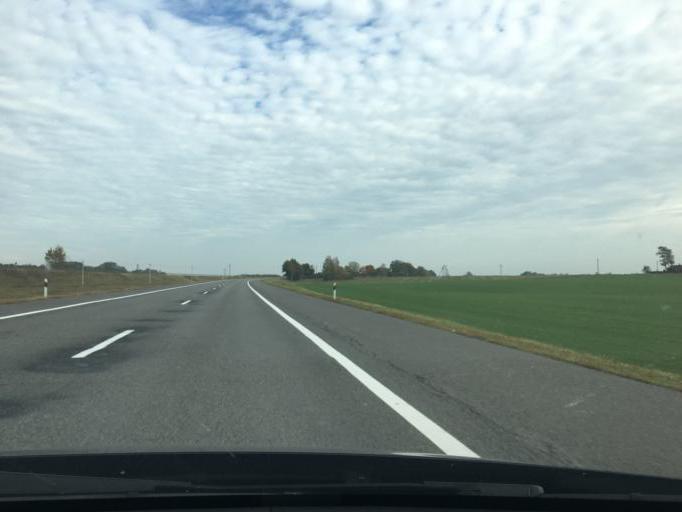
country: BY
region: Minsk
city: Dzyarzhynsk
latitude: 53.6772
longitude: 27.1897
